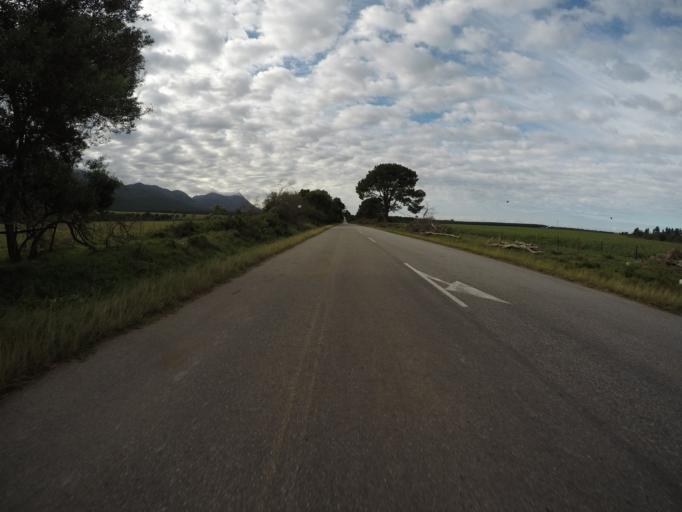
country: ZA
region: Eastern Cape
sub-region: Cacadu District Municipality
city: Kareedouw
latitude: -34.0209
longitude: 24.3559
